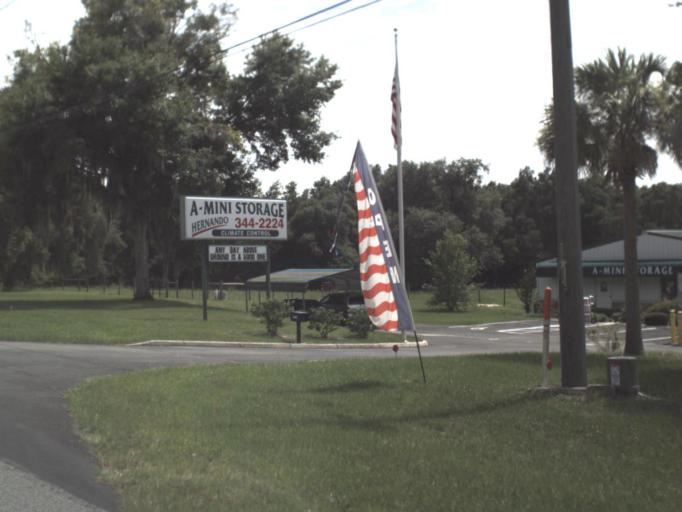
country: US
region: Florida
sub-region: Citrus County
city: Hernando
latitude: 28.9160
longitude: -82.3756
